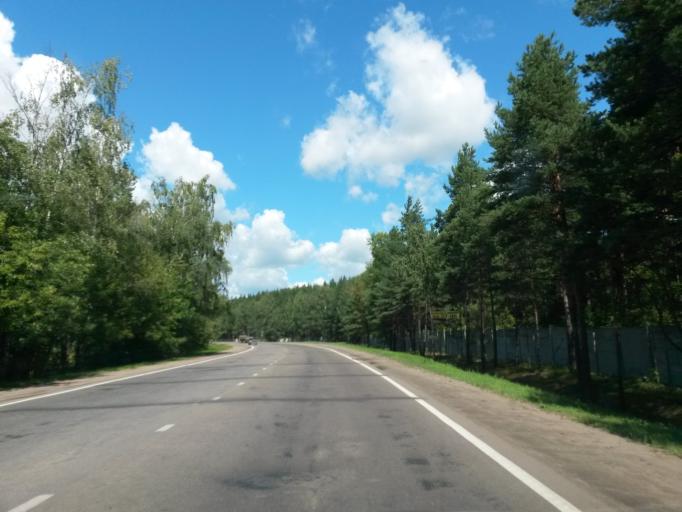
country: RU
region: Jaroslavl
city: Yaroslavl
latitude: 57.6726
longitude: 39.9083
